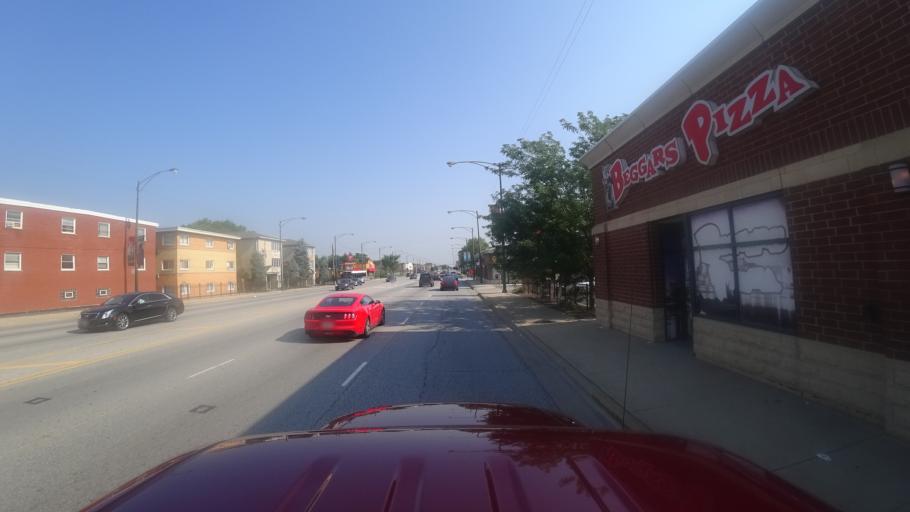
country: US
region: Illinois
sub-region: Cook County
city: Stickney
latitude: 41.7995
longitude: -87.7428
